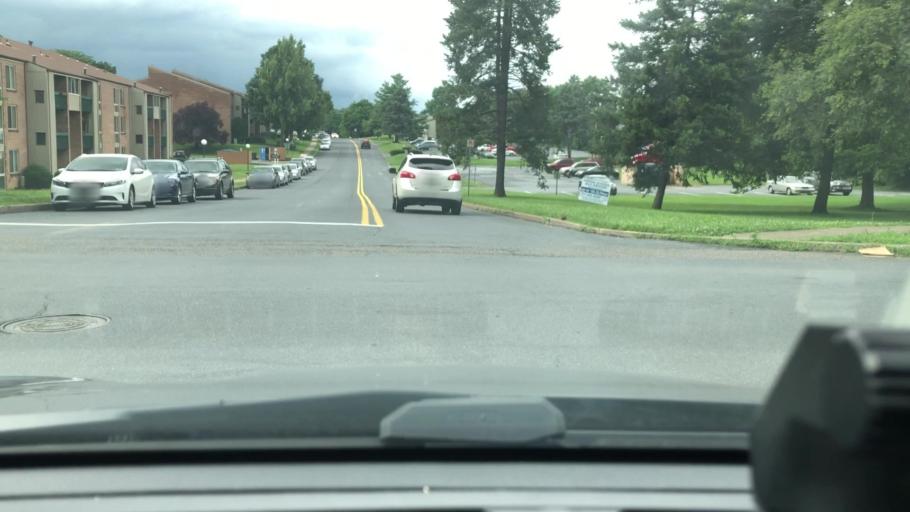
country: US
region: Pennsylvania
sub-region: Dauphin County
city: Colonial Park
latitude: 40.2838
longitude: -76.8093
